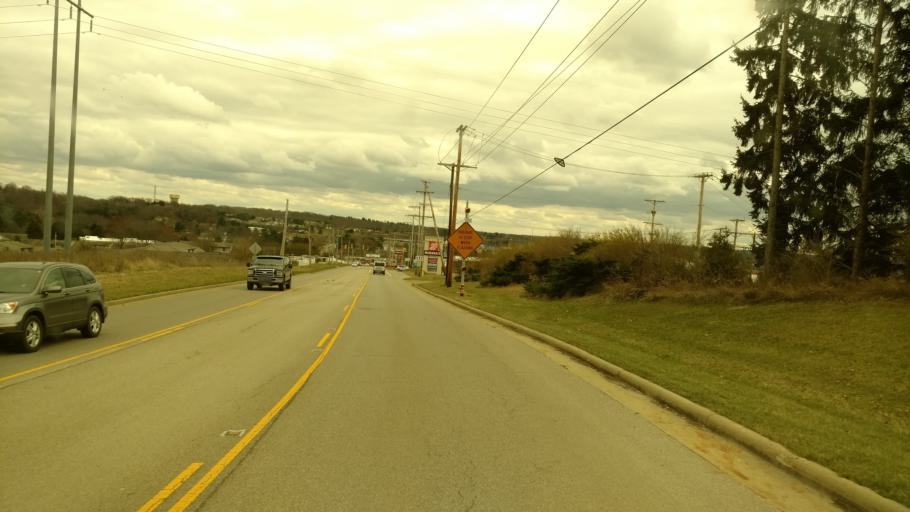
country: US
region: Ohio
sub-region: Muskingum County
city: North Zanesville
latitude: 39.9958
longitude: -82.0359
